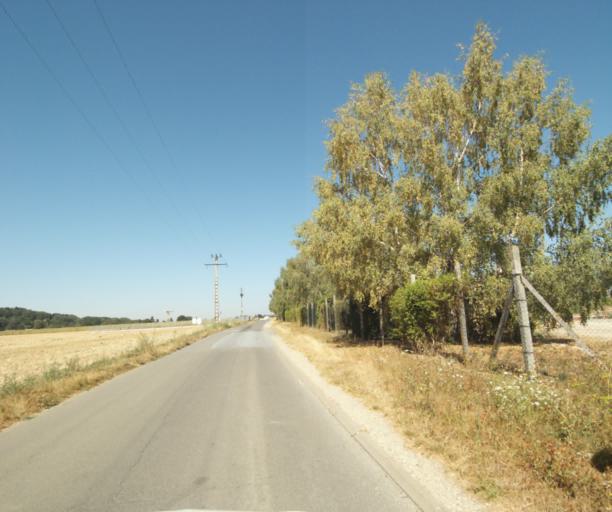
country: FR
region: Ile-de-France
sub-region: Departement de l'Essonne
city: Itteville
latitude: 48.5109
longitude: 2.3544
